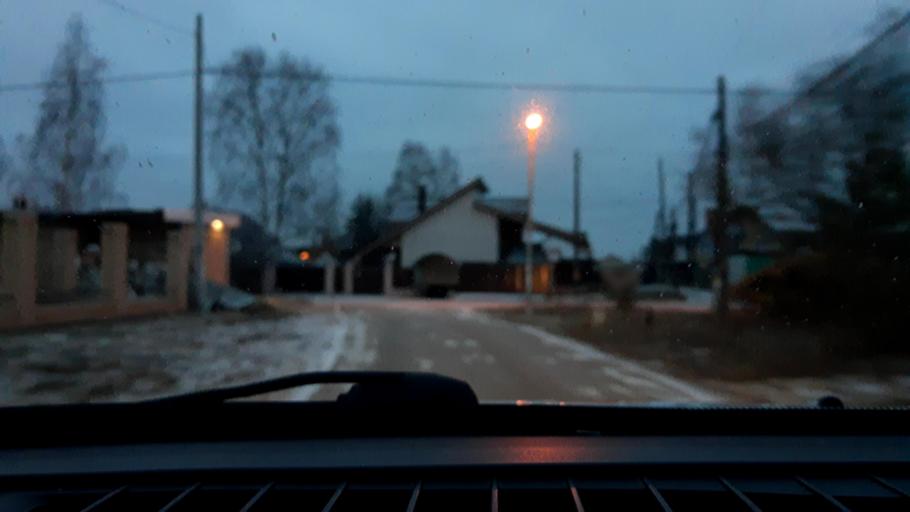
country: RU
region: Nizjnij Novgorod
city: Gorbatovka
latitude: 56.3865
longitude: 43.7516
